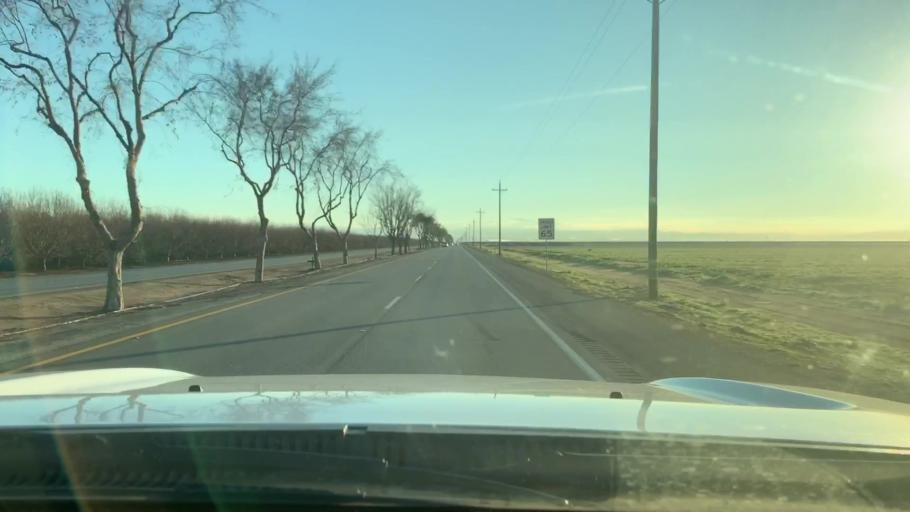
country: US
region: California
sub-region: Kern County
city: Shafter
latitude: 35.4997
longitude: -119.2407
